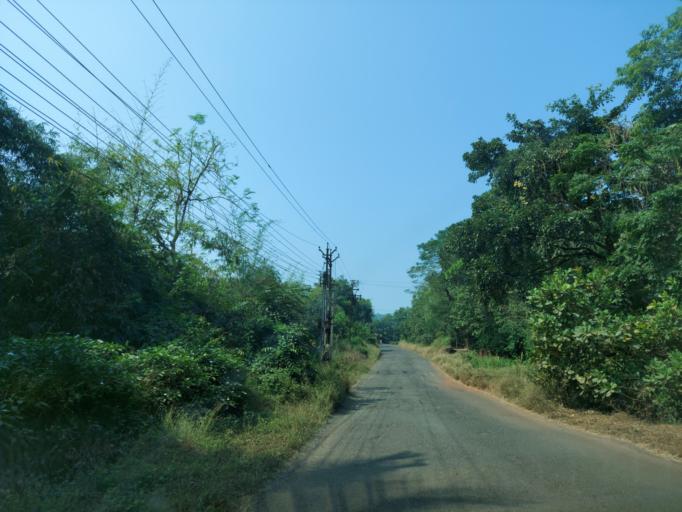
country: IN
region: Maharashtra
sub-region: Sindhudurg
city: Kudal
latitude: 15.9687
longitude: 73.6357
